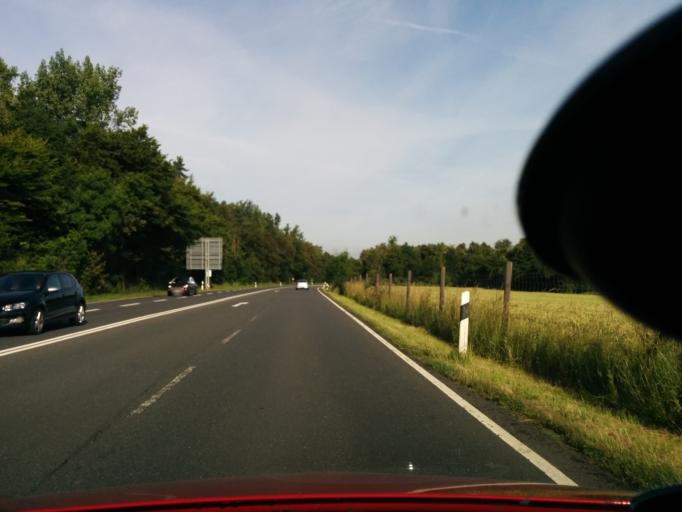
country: DE
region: Lower Saxony
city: Goslar
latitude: 51.9201
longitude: 10.3991
